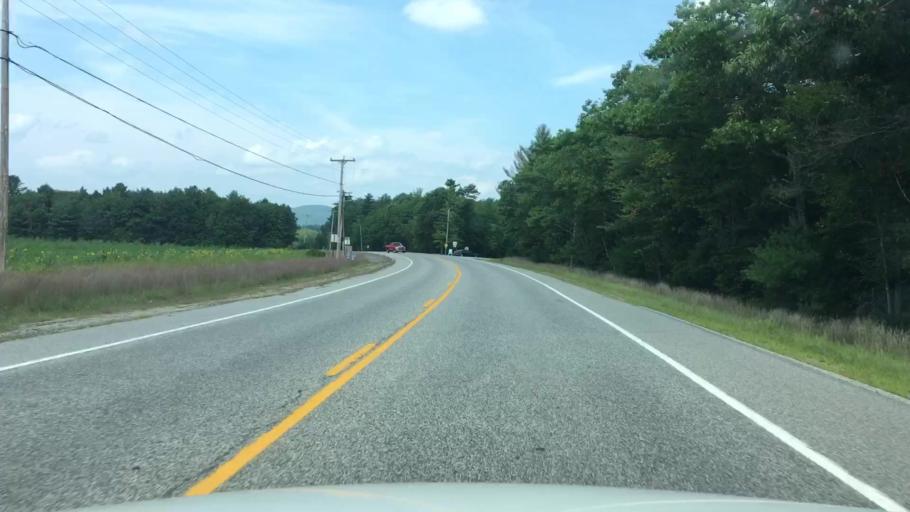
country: US
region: Maine
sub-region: Oxford County
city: Canton
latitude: 44.4648
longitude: -70.3213
